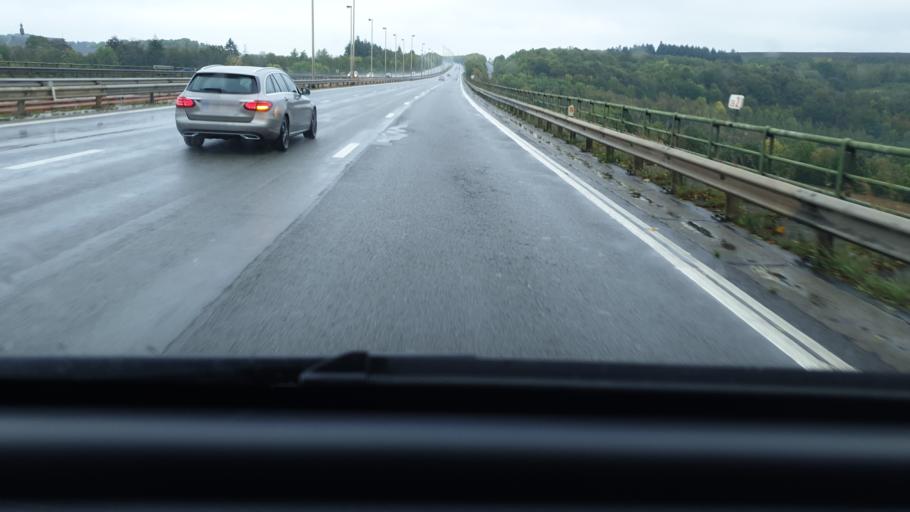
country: BE
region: Wallonia
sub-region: Province de Liege
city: Wanze
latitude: 50.5646
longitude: 5.1693
